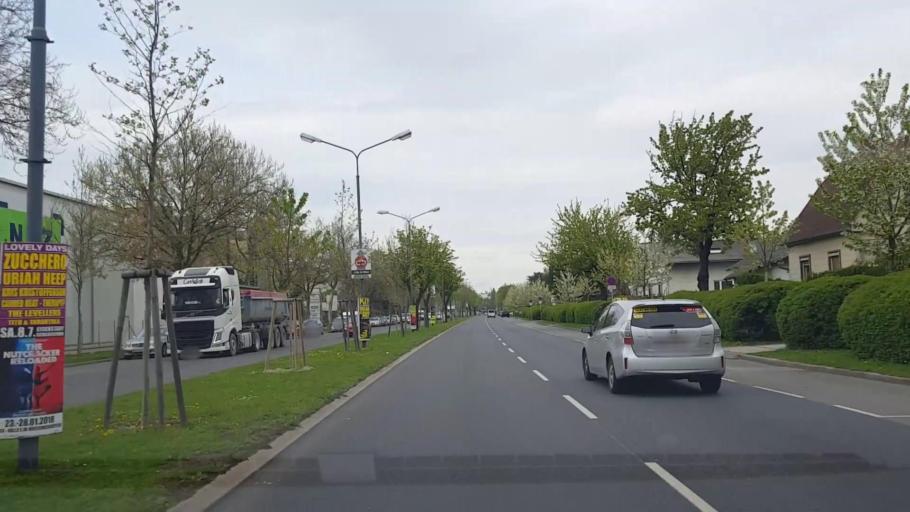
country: AT
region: Lower Austria
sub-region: Politischer Bezirk Modling
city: Vosendorf
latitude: 48.1408
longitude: 16.3593
